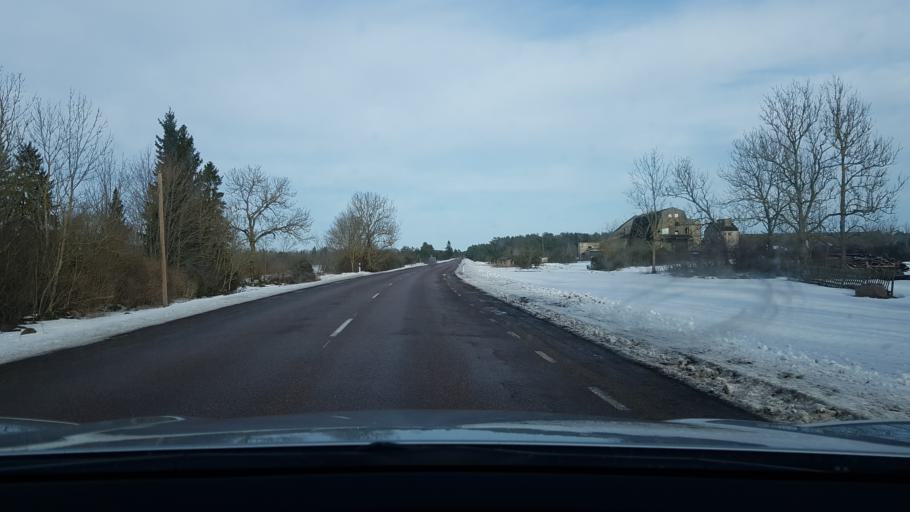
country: EE
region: Saare
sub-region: Kuressaare linn
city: Kuressaare
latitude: 58.3292
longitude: 22.5590
